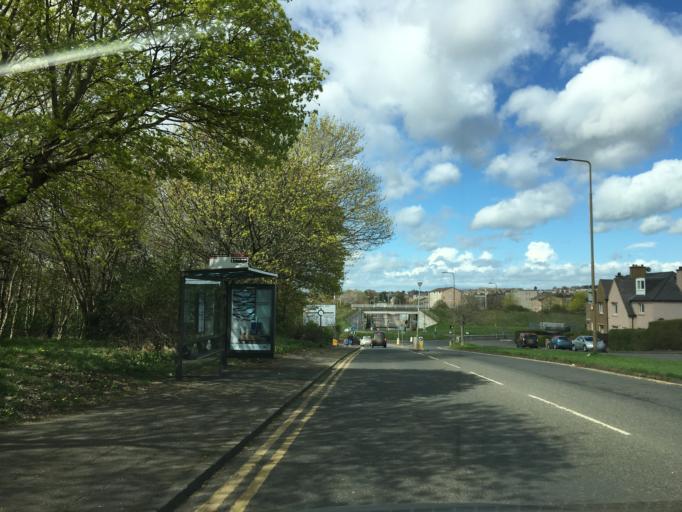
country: GB
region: Scotland
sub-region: Edinburgh
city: Colinton
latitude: 55.9283
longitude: -3.2845
